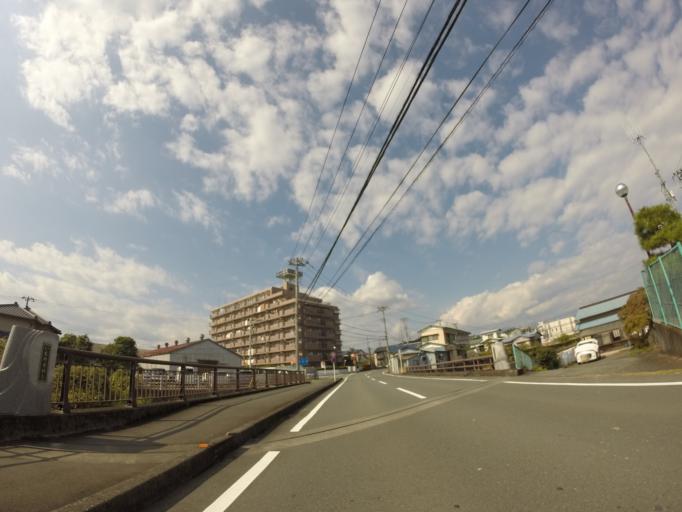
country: JP
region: Shizuoka
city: Fujinomiya
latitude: 35.2134
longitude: 138.6276
